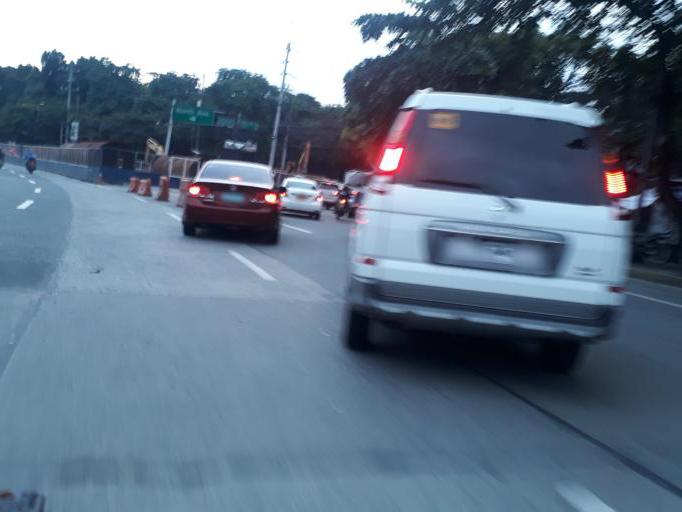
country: PH
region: Metro Manila
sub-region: Quezon City
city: Quezon City
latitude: 14.6530
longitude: 121.0466
